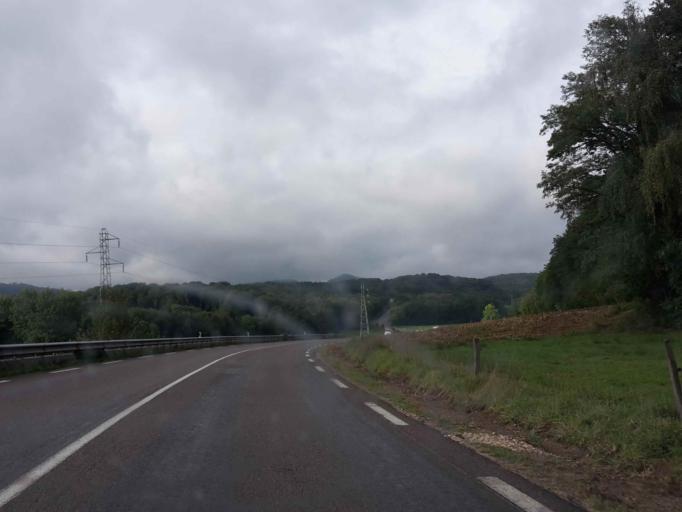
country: FR
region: Franche-Comte
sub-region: Departement du Doubs
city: Roulans
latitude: 47.3348
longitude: 6.2777
